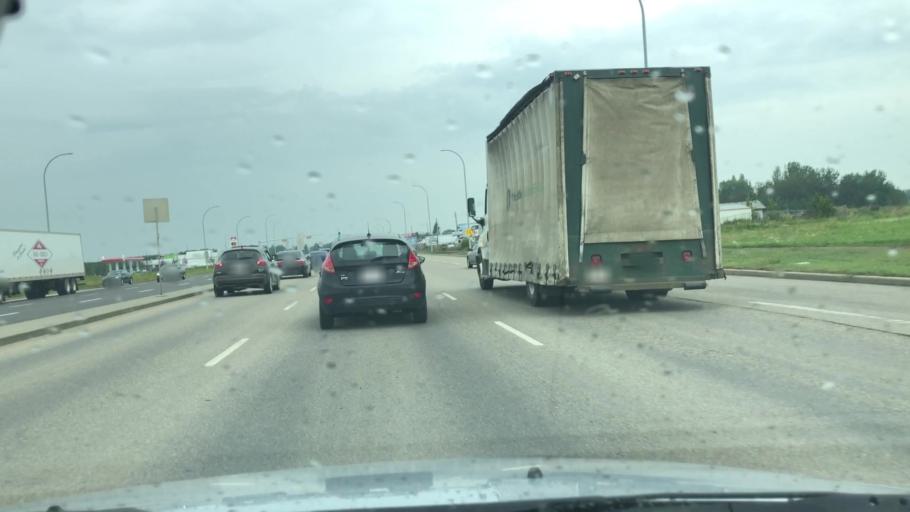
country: CA
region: Alberta
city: St. Albert
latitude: 53.6001
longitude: -113.5755
